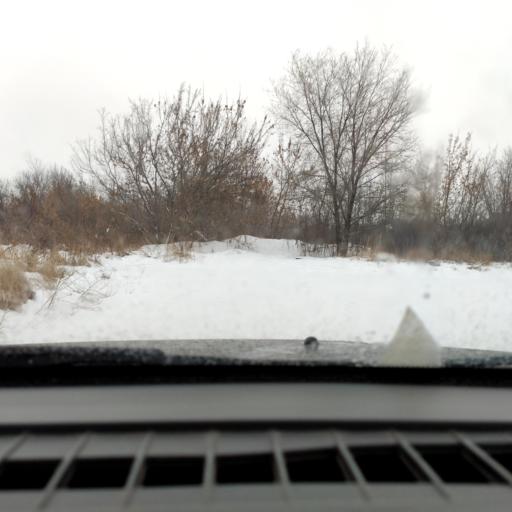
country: RU
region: Samara
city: Tol'yatti
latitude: 53.5626
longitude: 49.3283
